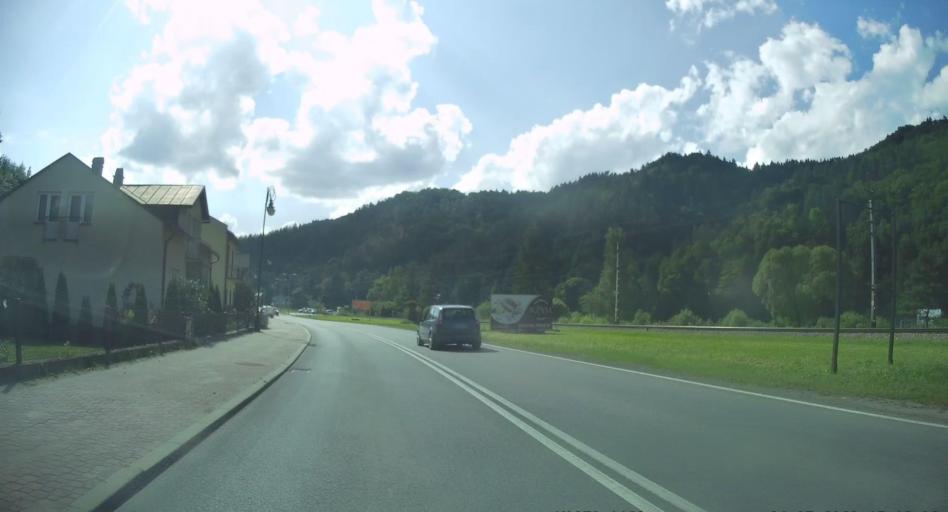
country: PL
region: Lesser Poland Voivodeship
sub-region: Powiat nowosadecki
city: Muszyna
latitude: 49.3598
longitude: 20.9055
